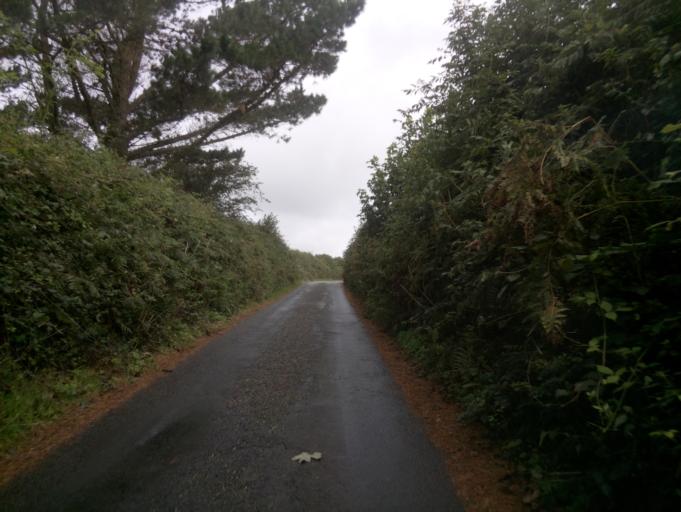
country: GB
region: England
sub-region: Devon
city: Dartmouth
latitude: 50.3325
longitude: -3.5853
